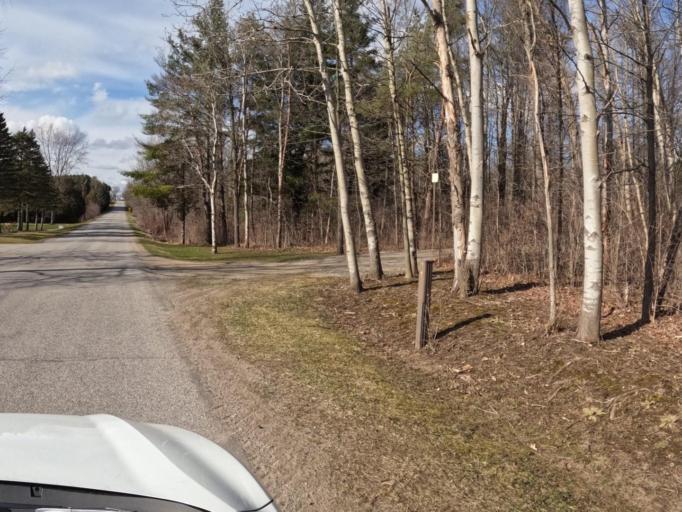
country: CA
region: Ontario
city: Norfolk County
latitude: 42.8916
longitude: -80.2858
